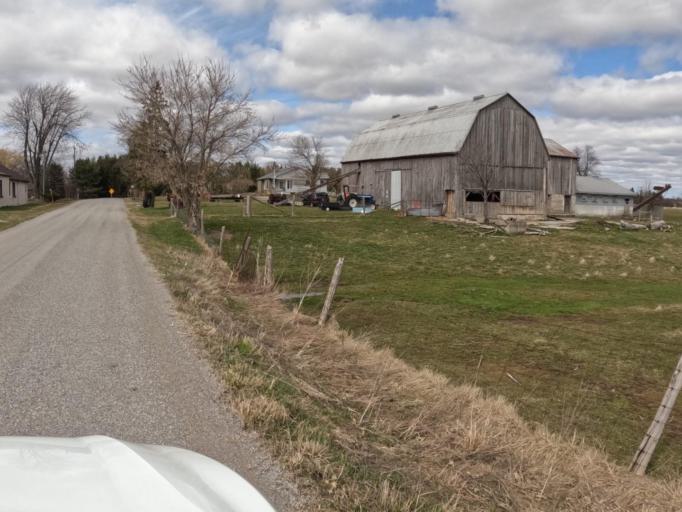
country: CA
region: Ontario
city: Norfolk County
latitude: 42.8651
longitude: -80.1756
